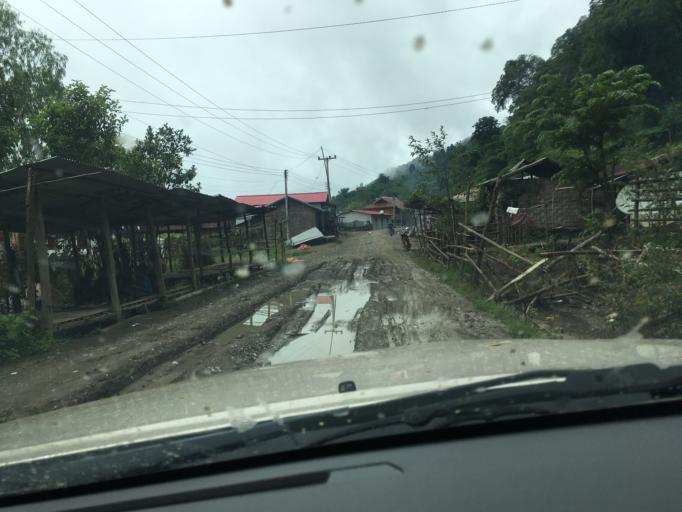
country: LA
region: Phongsali
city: Phongsali
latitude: 21.4461
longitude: 102.1610
